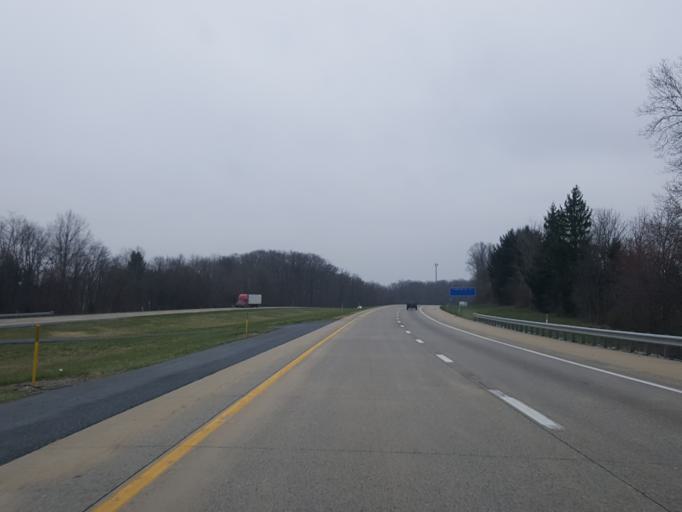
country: US
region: Pennsylvania
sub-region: Lebanon County
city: Jonestown
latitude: 40.4718
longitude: -76.5208
